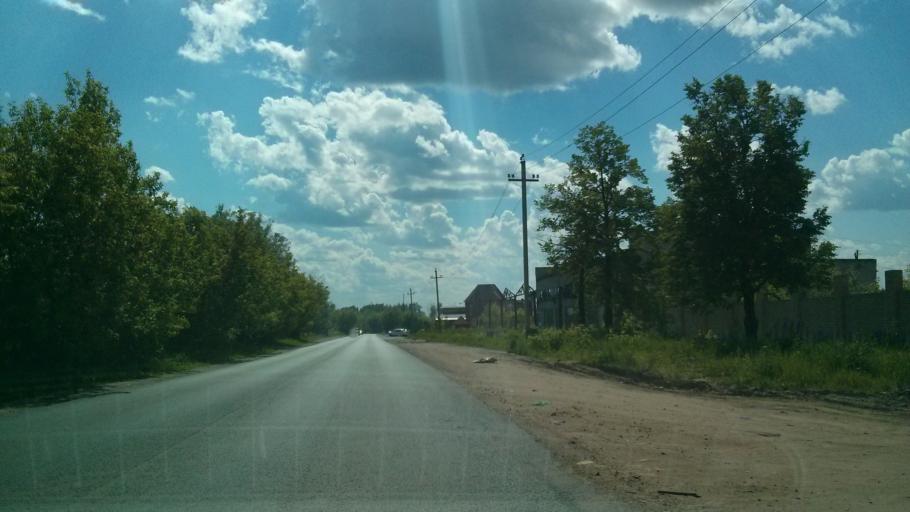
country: RU
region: Vladimir
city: Murom
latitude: 55.5548
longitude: 42.0074
